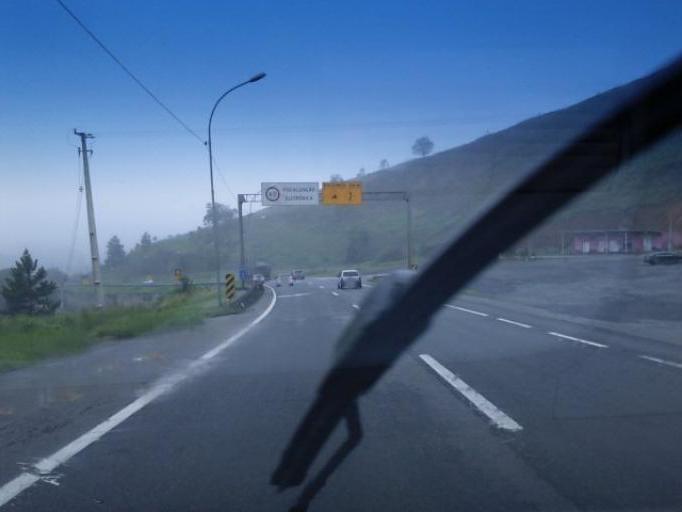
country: BR
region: Parana
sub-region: Campina Grande Do Sul
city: Campina Grande do Sul
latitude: -25.1115
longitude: -48.8110
